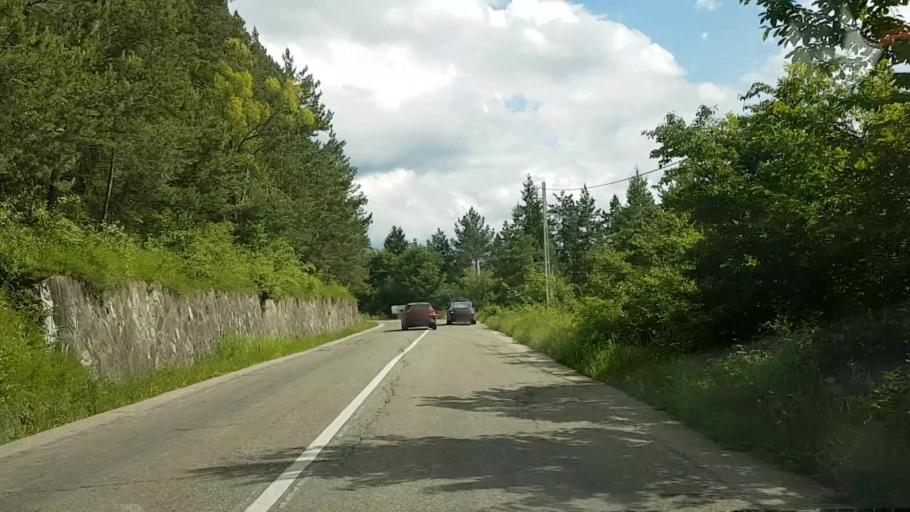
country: RO
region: Neamt
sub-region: Comuna Hangu
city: Hangu
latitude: 47.0111
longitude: 26.0846
